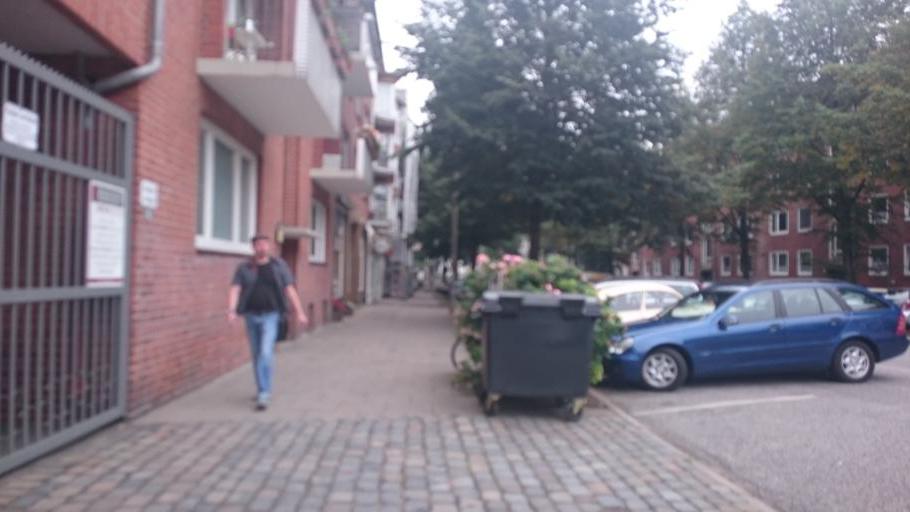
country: DE
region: Hamburg
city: Stellingen
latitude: 53.5792
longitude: 9.9495
